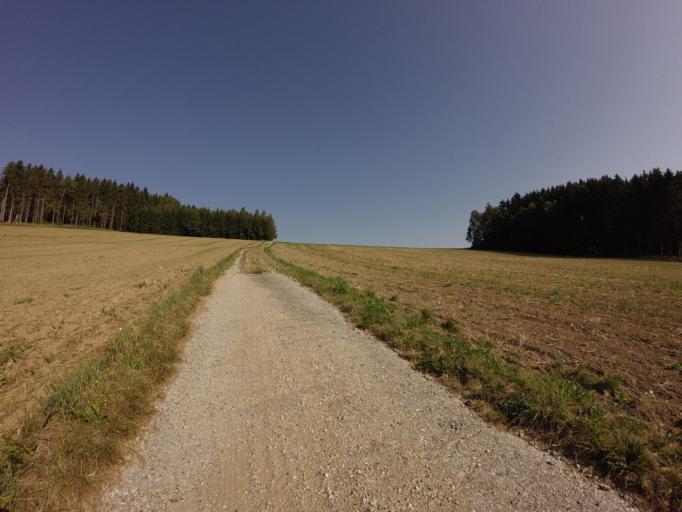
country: AT
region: Upper Austria
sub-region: Politischer Bezirk Urfahr-Umgebung
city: Bad Leonfelden
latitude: 48.5497
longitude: 14.3228
